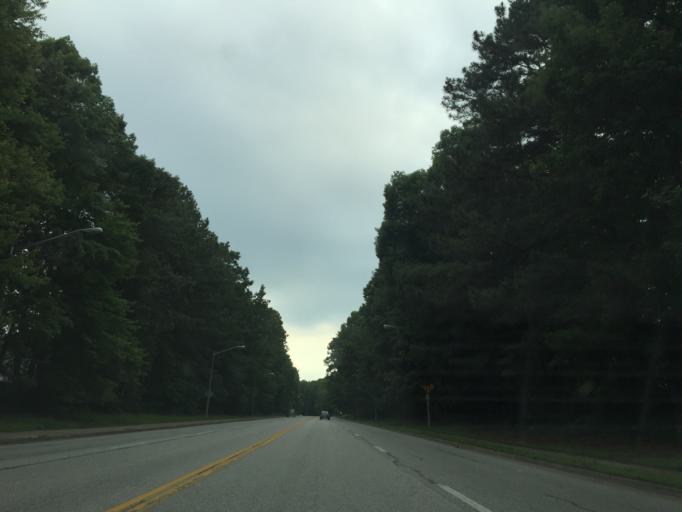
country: US
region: Virginia
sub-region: York County
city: Yorktown
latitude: 37.1028
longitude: -76.5179
